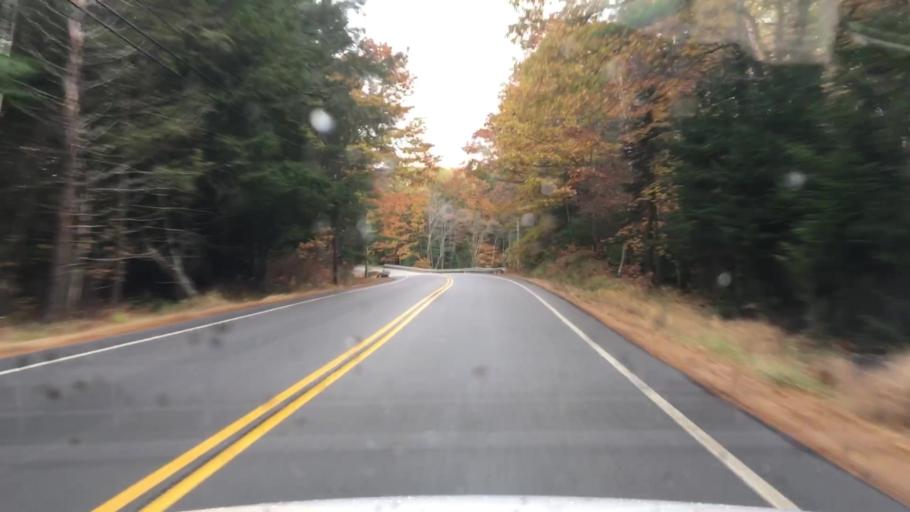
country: US
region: Maine
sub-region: Lincoln County
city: Jefferson
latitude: 44.2051
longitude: -69.5027
